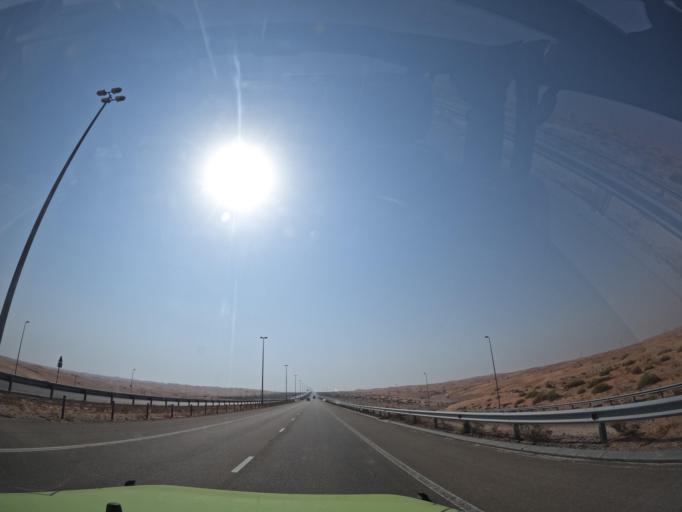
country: OM
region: Al Buraimi
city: Al Buraymi
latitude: 24.4396
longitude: 55.6662
